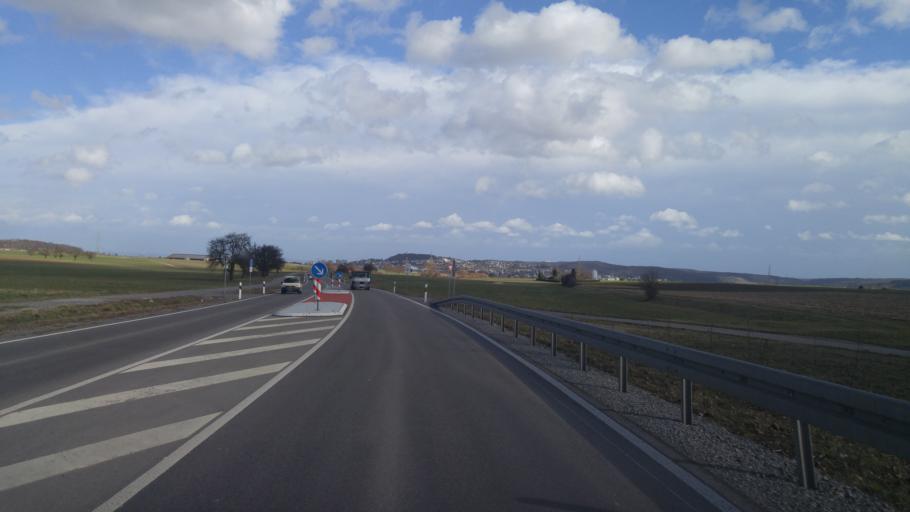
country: DE
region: Baden-Wuerttemberg
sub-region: Regierungsbezirk Stuttgart
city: Rutesheim
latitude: 48.8052
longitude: 8.9633
